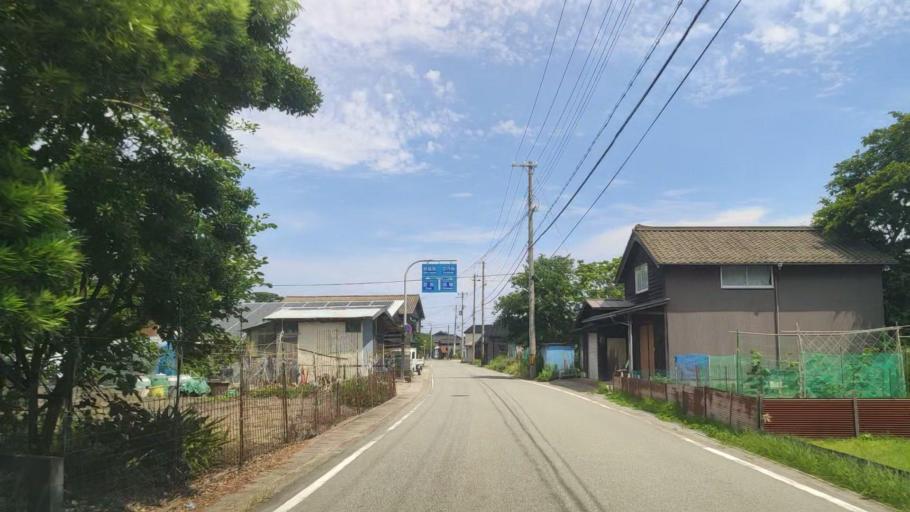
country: JP
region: Hyogo
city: Toyooka
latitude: 35.6548
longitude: 134.7628
